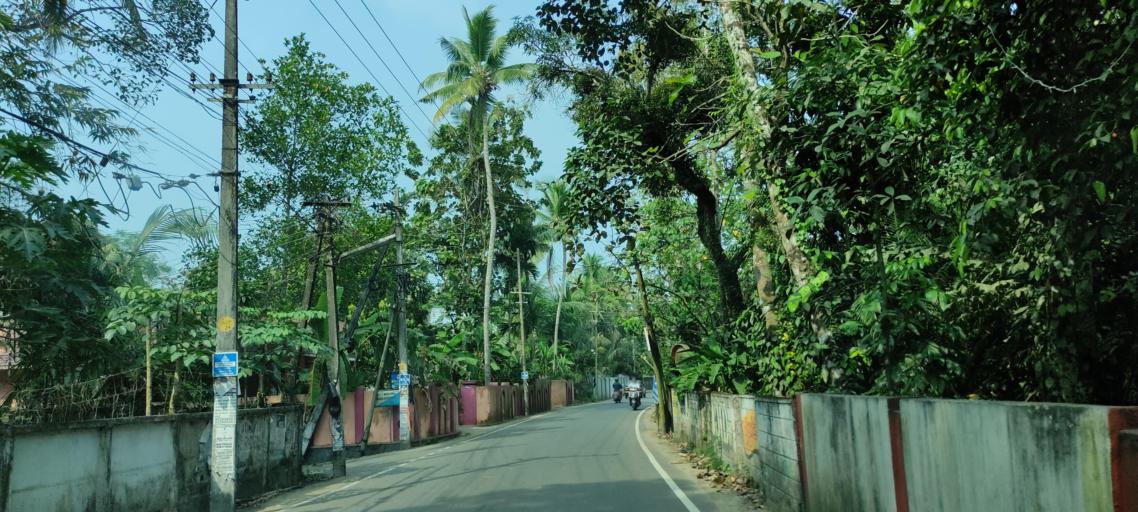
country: IN
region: Kerala
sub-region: Kottayam
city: Vaikam
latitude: 9.7439
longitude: 76.4015
